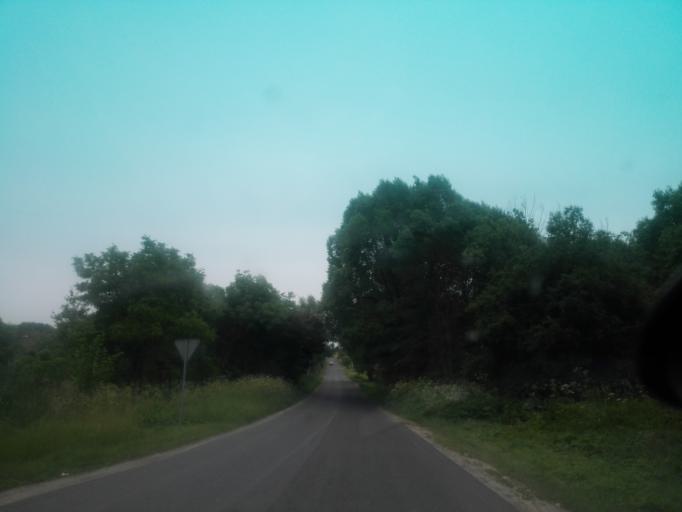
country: PL
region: Silesian Voivodeship
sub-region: Powiat czestochowski
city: Mstow
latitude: 50.7937
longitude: 19.3400
